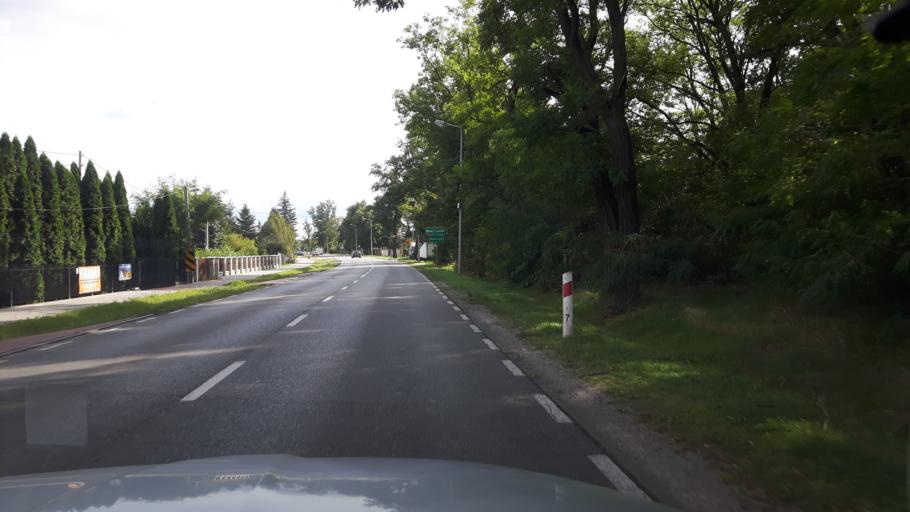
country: PL
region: Masovian Voivodeship
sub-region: Powiat wolominski
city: Kobylka
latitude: 52.3784
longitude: 21.2140
